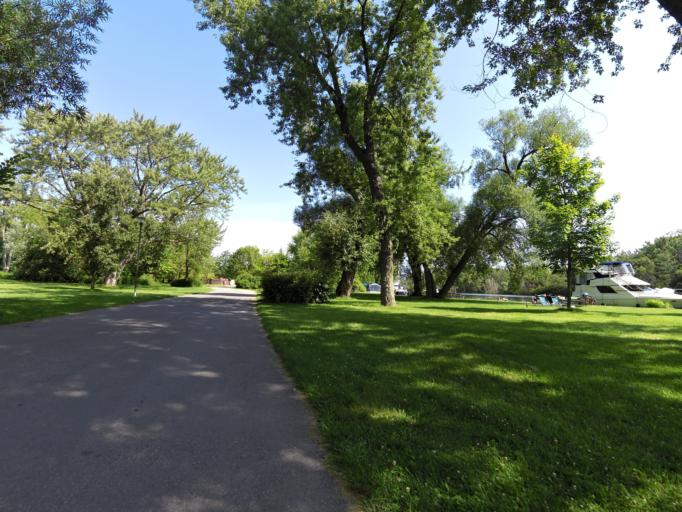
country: CA
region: Ontario
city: Toronto
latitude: 43.6176
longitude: -79.3906
